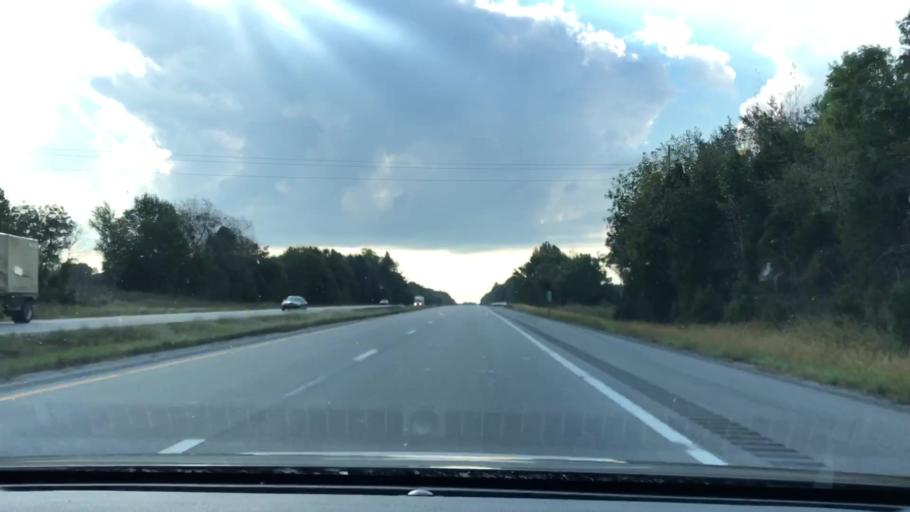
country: US
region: Kentucky
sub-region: Barren County
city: Cave City
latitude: 37.0305
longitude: -86.0502
